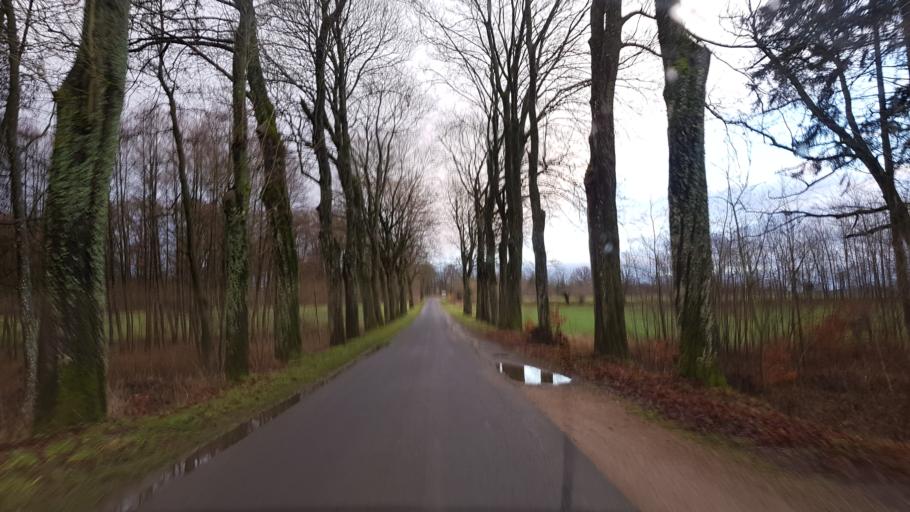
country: PL
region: West Pomeranian Voivodeship
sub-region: Powiat swidwinski
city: Rabino
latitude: 53.9479
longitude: 15.9138
